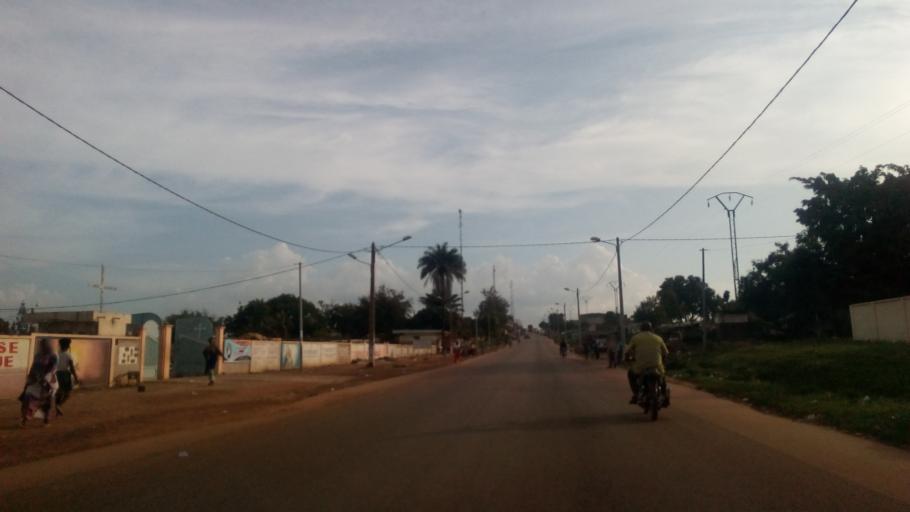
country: CI
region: Dix-Huit Montagnes
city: Duekoue
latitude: 6.7406
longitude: -7.3429
